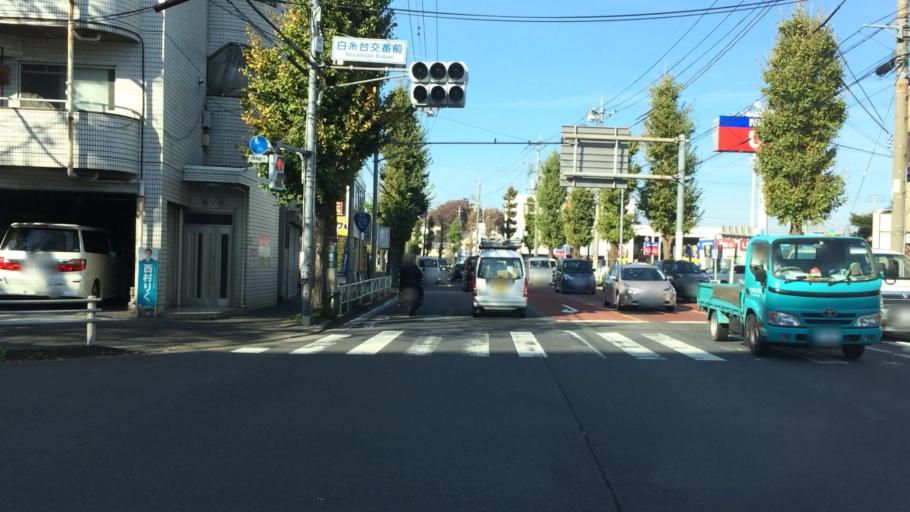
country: JP
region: Tokyo
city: Chofugaoka
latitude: 35.6699
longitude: 139.5088
